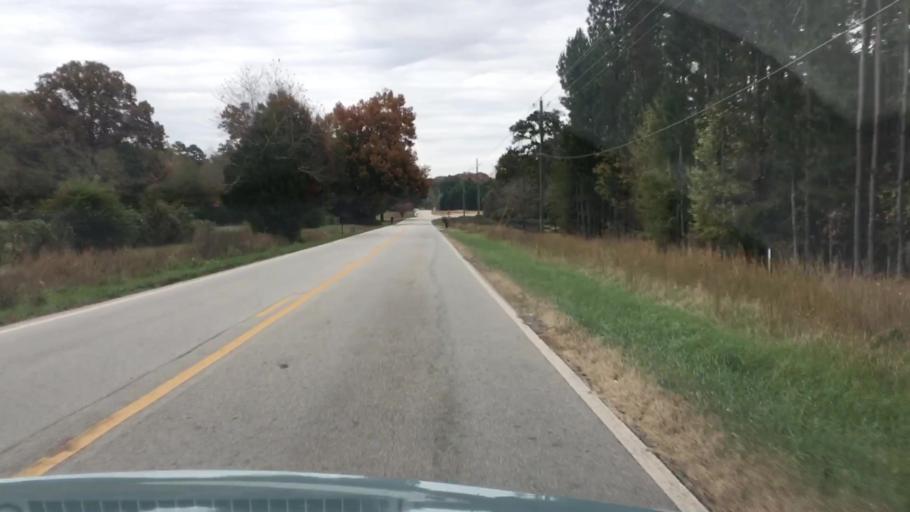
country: US
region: Georgia
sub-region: Henry County
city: McDonough
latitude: 33.5073
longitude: -84.1110
